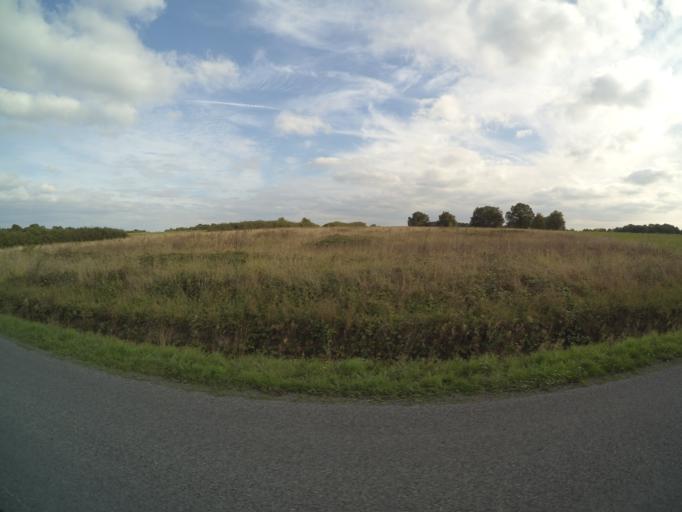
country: FR
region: Centre
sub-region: Departement d'Indre-et-Loire
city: Nazelles-Negron
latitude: 47.4396
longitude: 0.9531
